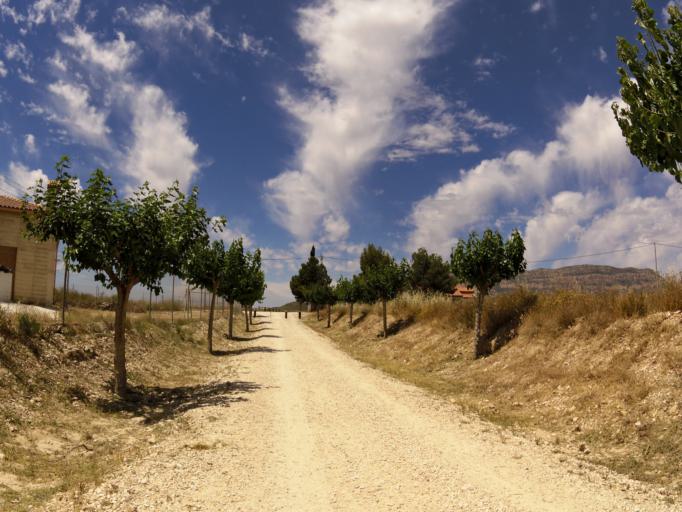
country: ES
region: Valencia
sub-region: Provincia de Alicante
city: Agost
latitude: 38.4430
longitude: -0.6568
